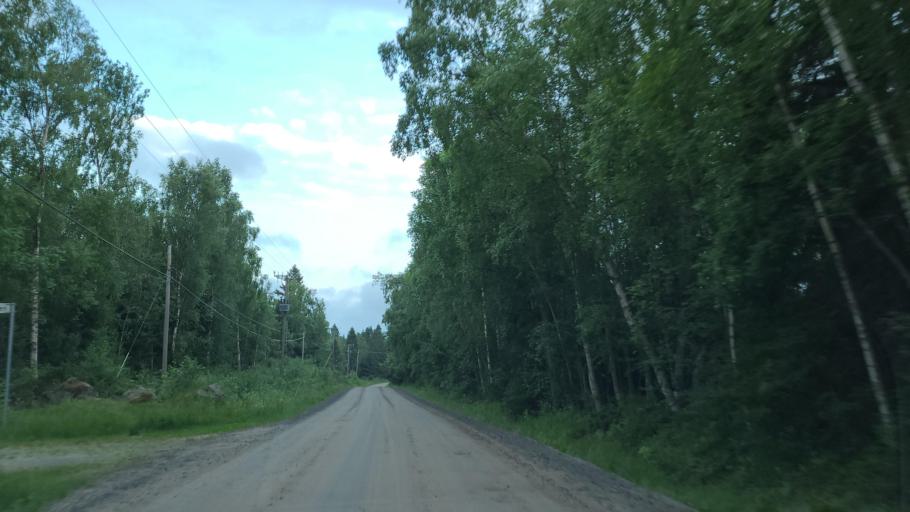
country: FI
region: Ostrobothnia
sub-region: Vaasa
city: Replot
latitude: 63.3057
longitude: 21.1541
